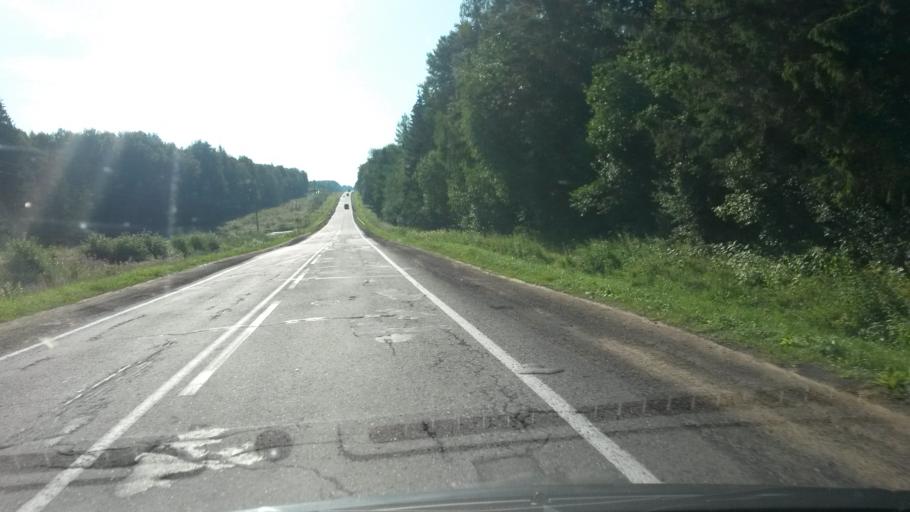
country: RU
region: Jaroslavl
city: Gavrilov-Yam
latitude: 57.2607
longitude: 40.0513
